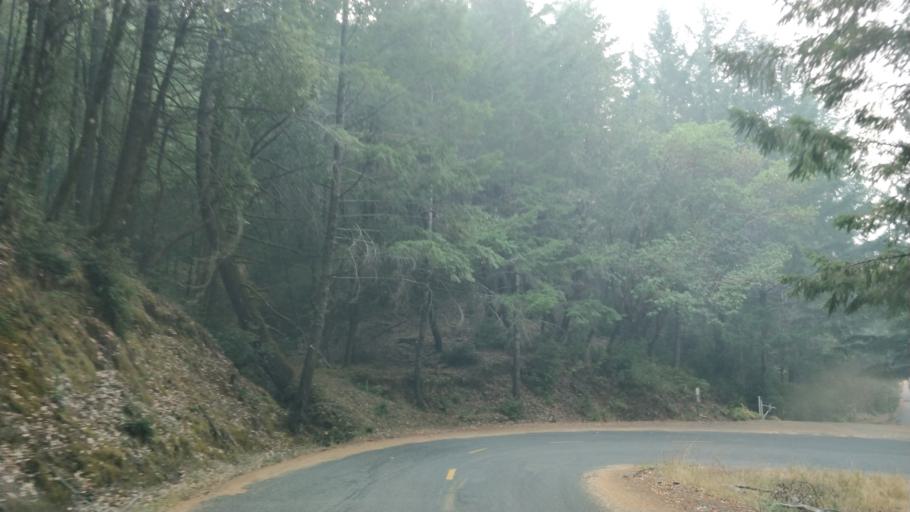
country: US
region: California
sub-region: Humboldt County
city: Rio Dell
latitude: 40.3324
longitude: -124.0359
